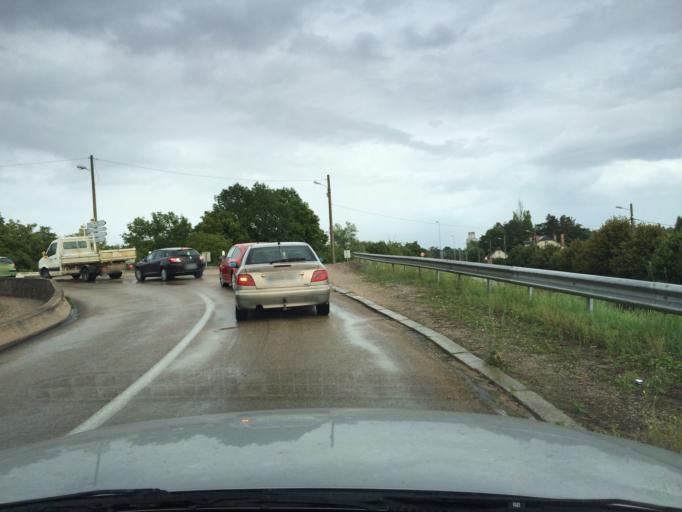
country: FR
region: Bourgogne
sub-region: Departement de l'Yonne
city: Joigny
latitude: 47.9735
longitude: 3.3972
